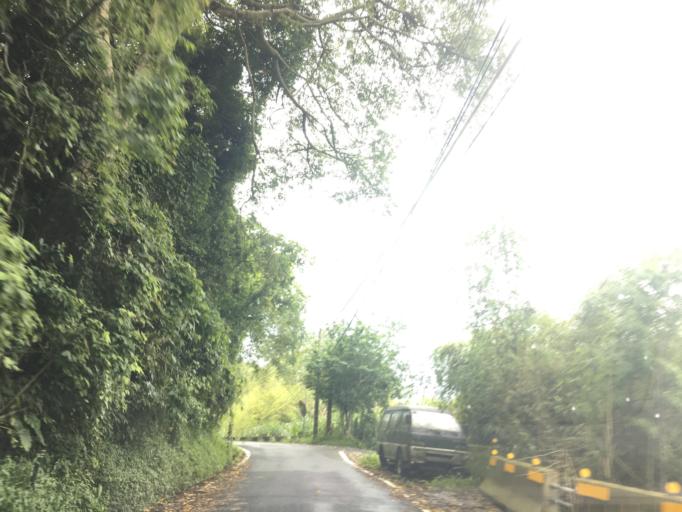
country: TW
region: Taiwan
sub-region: Yunlin
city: Douliu
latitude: 23.5521
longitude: 120.6738
